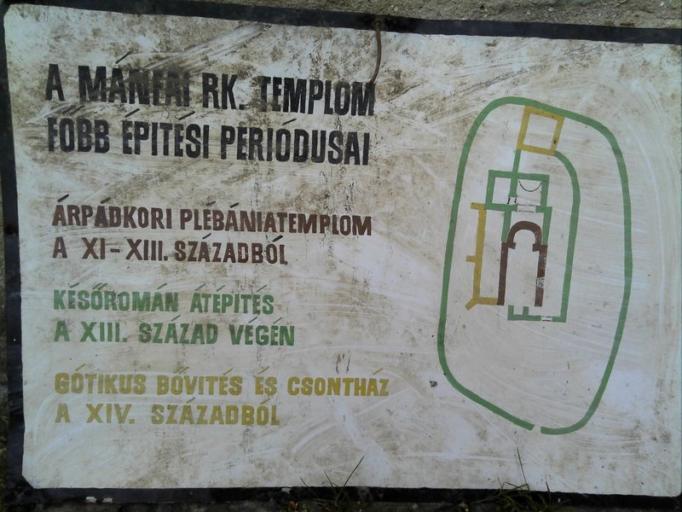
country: HU
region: Baranya
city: Komlo
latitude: 46.1583
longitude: 18.2264
